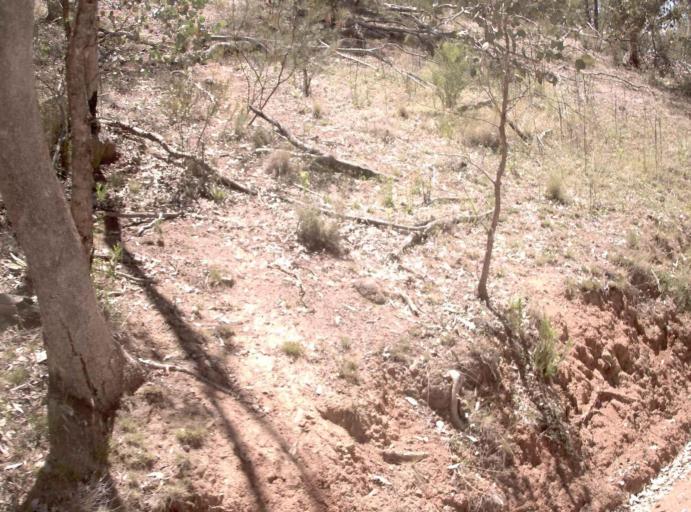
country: AU
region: New South Wales
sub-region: Snowy River
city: Jindabyne
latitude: -37.0865
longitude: 148.4131
